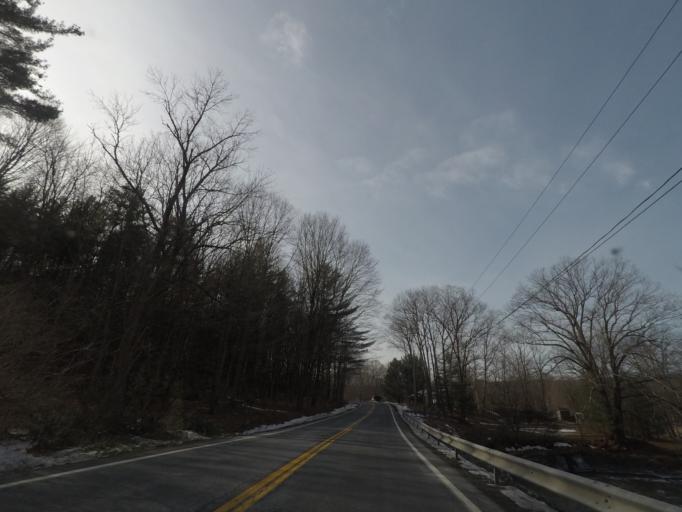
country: US
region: New York
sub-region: Rensselaer County
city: Nassau
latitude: 42.4907
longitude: -73.5510
